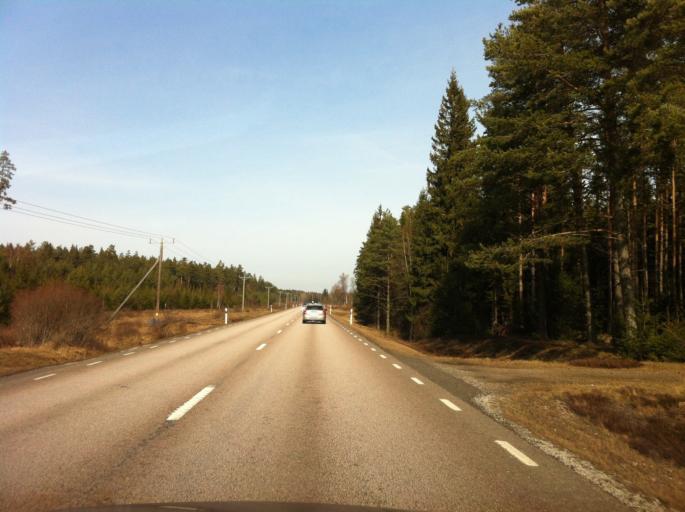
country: SE
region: Joenkoeping
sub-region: Mullsjo Kommun
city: Mullsjoe
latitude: 58.0618
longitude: 13.8587
